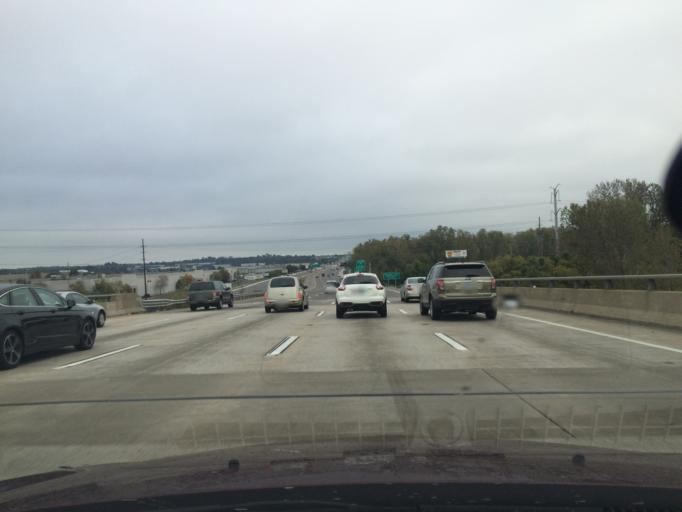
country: US
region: Missouri
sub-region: Saint Charles County
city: Saint Charles
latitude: 38.7627
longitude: -90.4793
